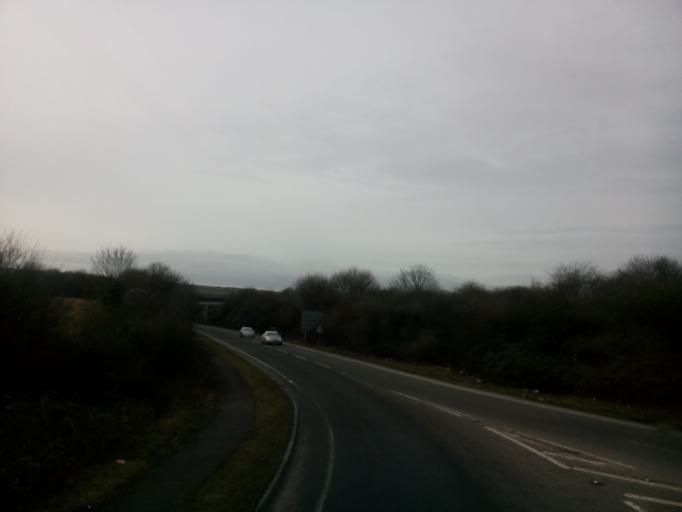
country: GB
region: England
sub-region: Hampshire
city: Winchester
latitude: 51.0591
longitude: -1.2922
